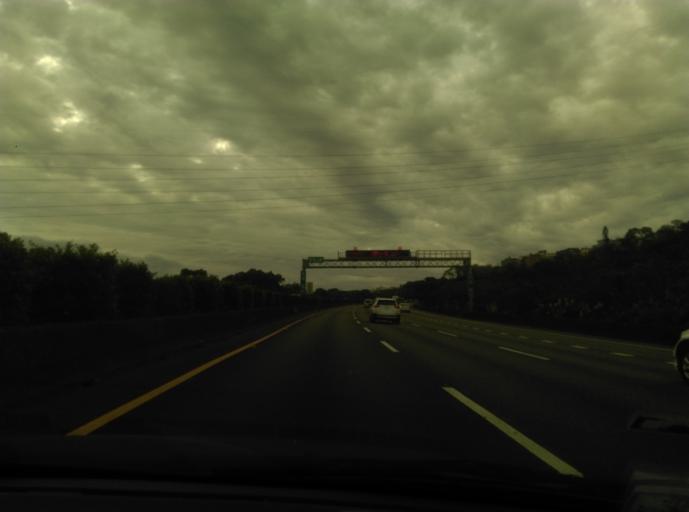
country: TW
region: Taiwan
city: Daxi
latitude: 24.9120
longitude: 121.2924
